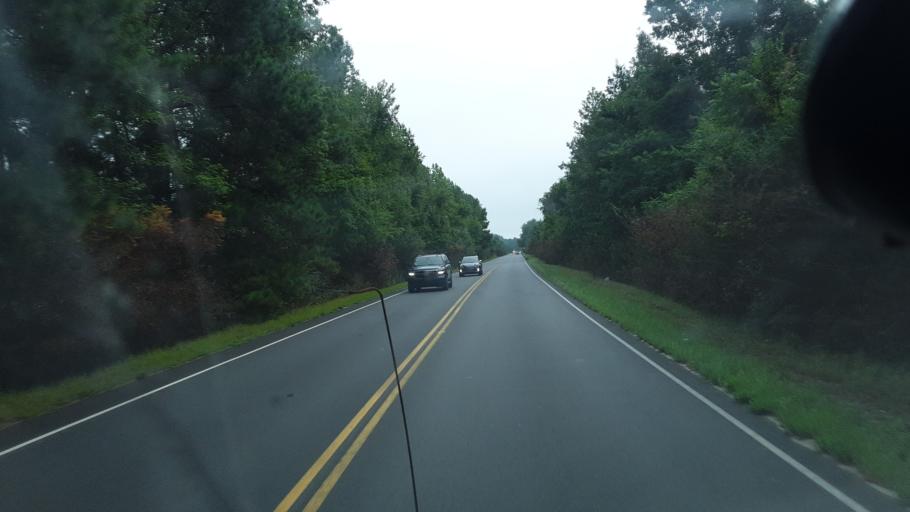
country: US
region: South Carolina
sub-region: Florence County
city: Johnsonville
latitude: 33.8954
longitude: -79.4459
